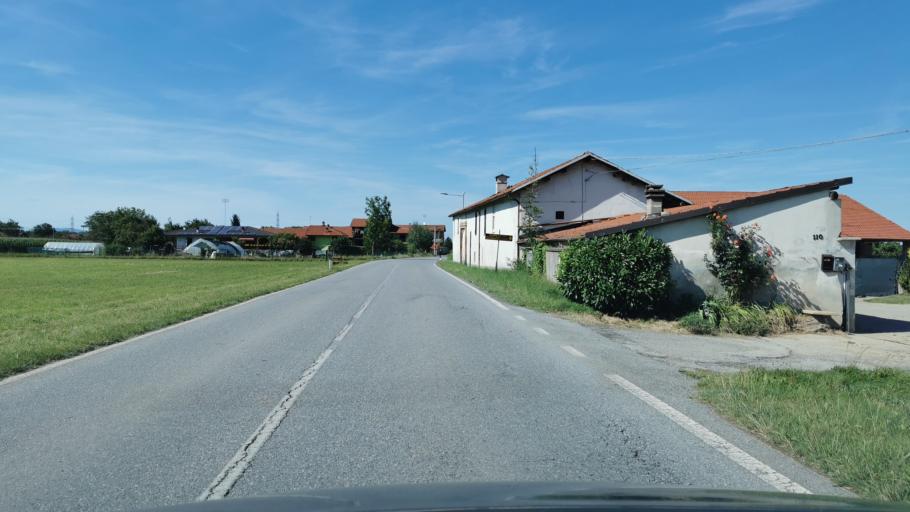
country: IT
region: Piedmont
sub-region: Provincia di Cuneo
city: Boves
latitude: 44.3461
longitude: 7.5580
